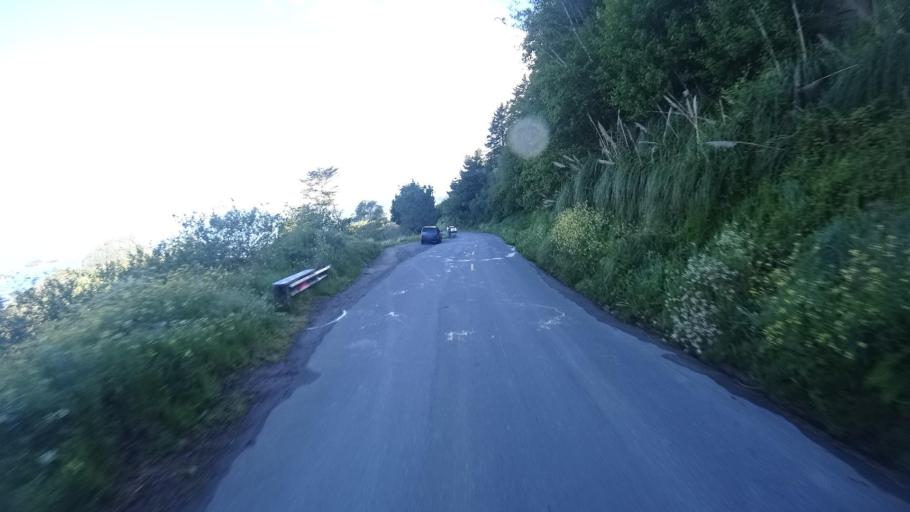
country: US
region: California
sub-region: Humboldt County
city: Westhaven-Moonstone
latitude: 41.0357
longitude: -124.1170
